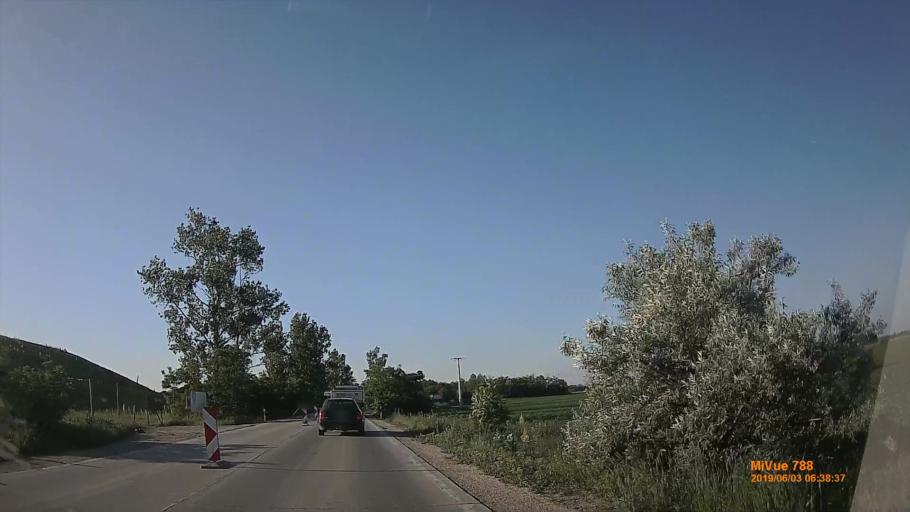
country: HU
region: Pest
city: Dunavarsany
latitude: 47.2938
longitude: 19.0948
